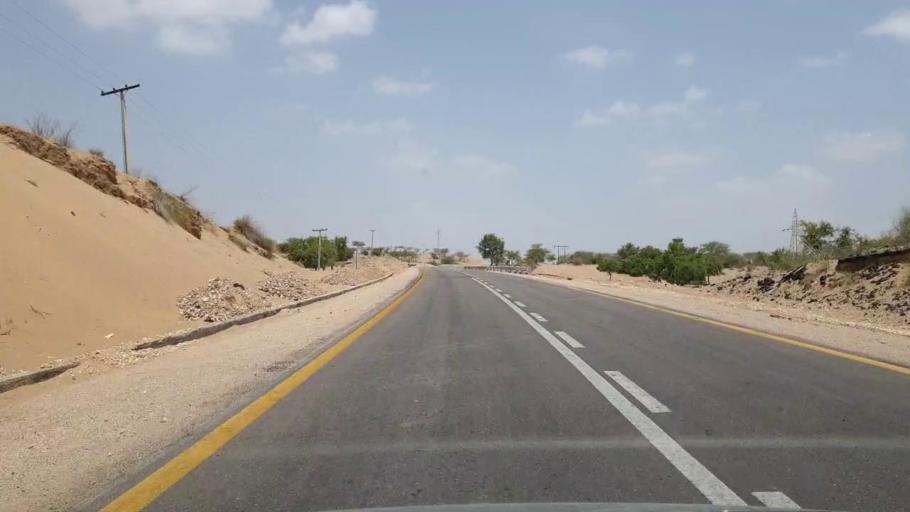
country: PK
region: Sindh
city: Mithi
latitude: 24.8151
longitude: 69.7055
